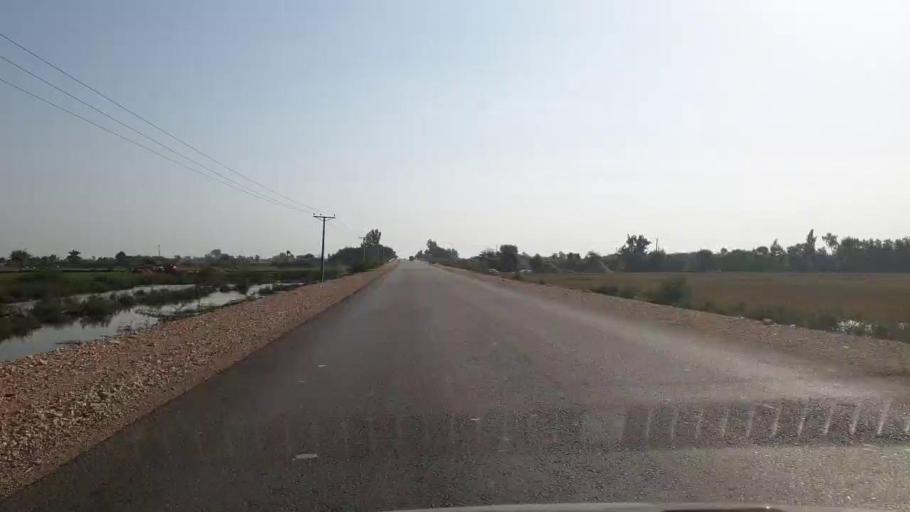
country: PK
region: Sindh
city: Tando Bago
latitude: 24.6580
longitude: 68.9694
